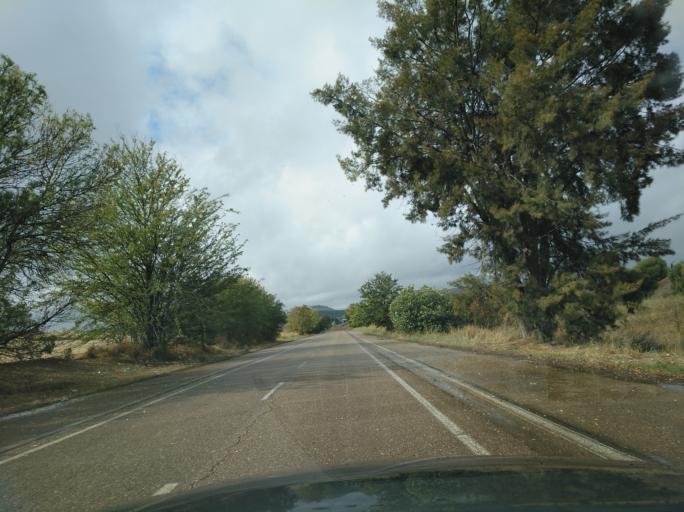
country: PT
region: Portalegre
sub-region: Elvas
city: Elvas
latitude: 38.8887
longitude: -7.1110
